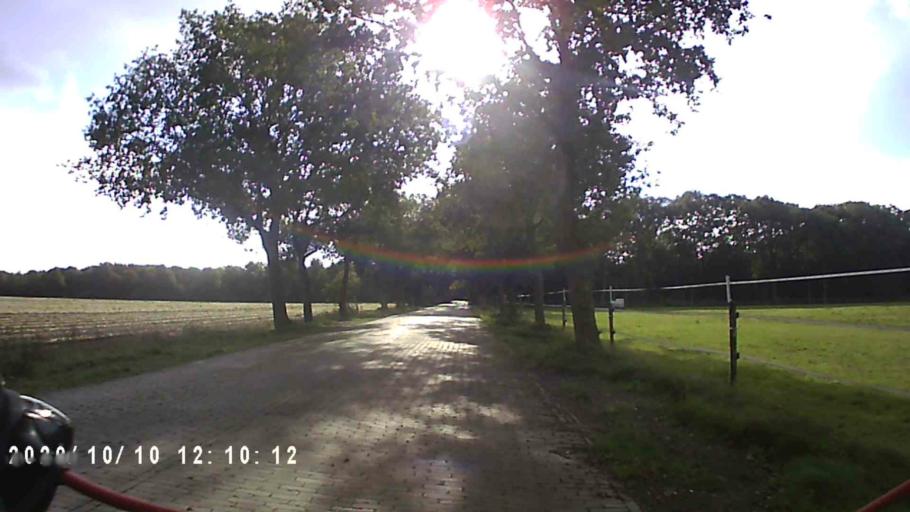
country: NL
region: Friesland
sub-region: Gemeente Heerenveen
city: Jubbega
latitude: 53.0435
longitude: 6.1465
